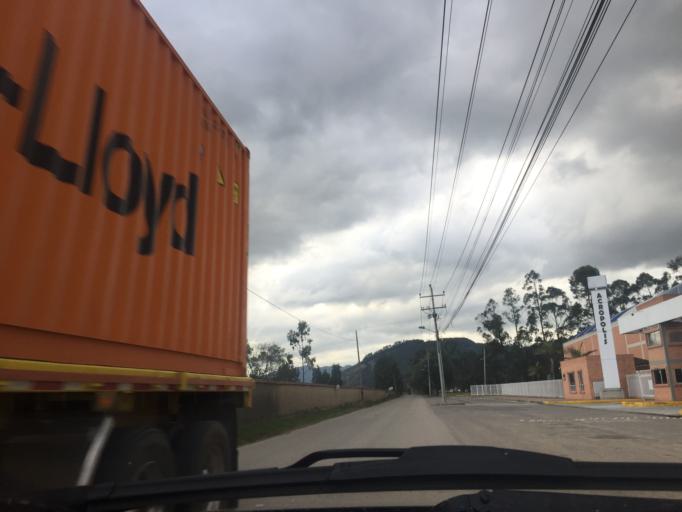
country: CO
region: Cundinamarca
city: Sopo
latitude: 4.9374
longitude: -73.9450
